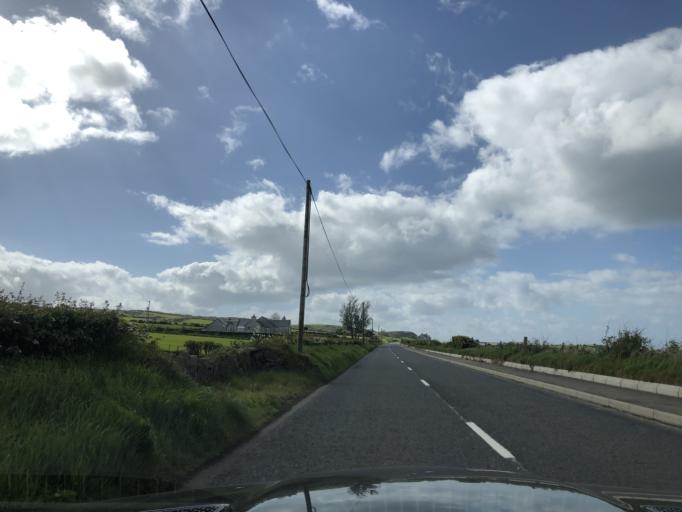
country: GB
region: Northern Ireland
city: Bushmills
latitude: 55.2081
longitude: -6.5421
